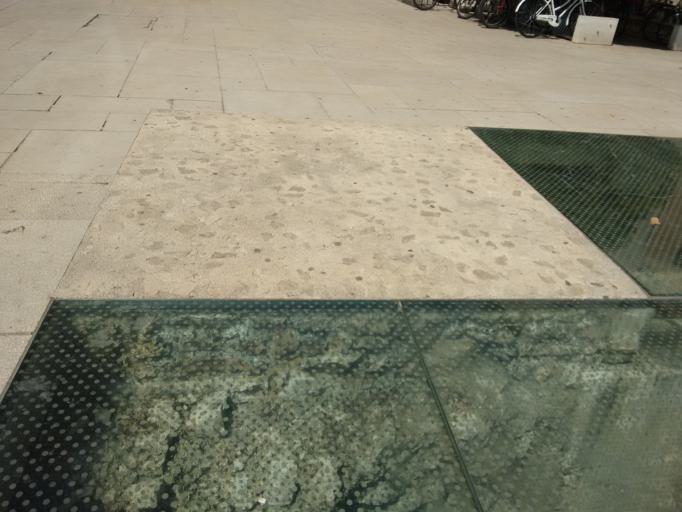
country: HR
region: Zadarska
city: Zadar
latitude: 44.1128
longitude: 15.2289
